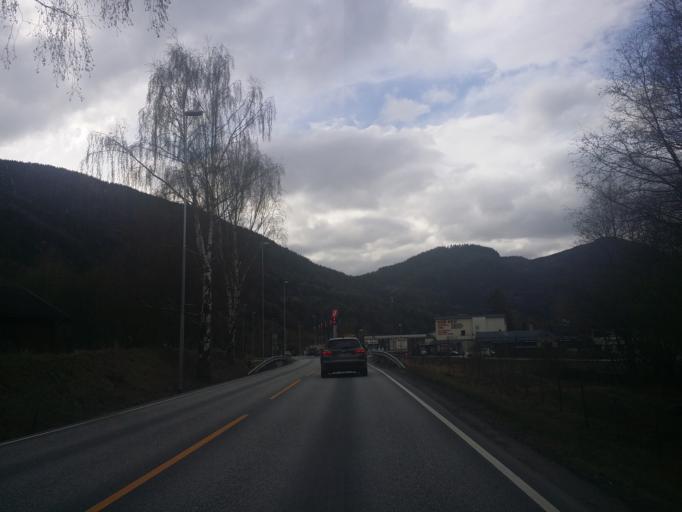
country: NO
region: Buskerud
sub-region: Nes
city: Nesbyen
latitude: 60.4870
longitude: 9.1934
